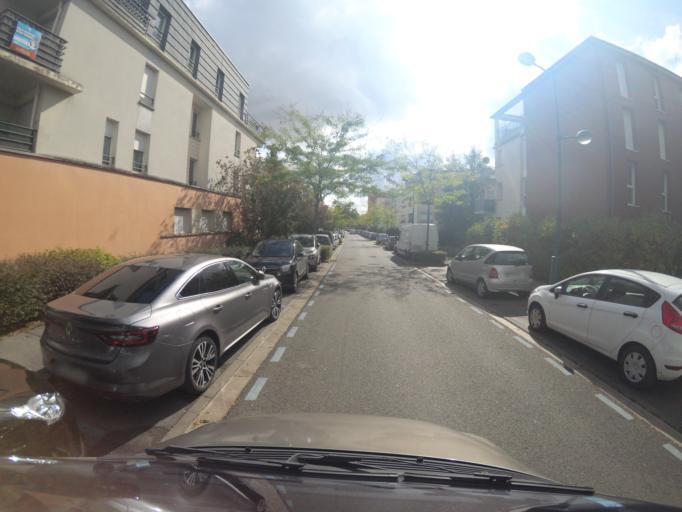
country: FR
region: Ile-de-France
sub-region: Departement de Seine-et-Marne
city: Montevrain
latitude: 48.8545
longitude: 2.7626
